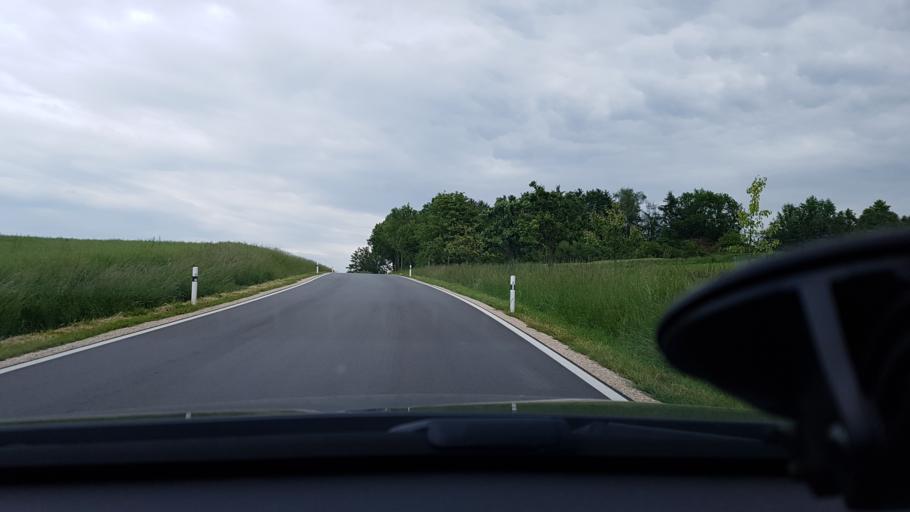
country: DE
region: Bavaria
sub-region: Lower Bavaria
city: Triftern
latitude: 48.3881
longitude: 13.0053
